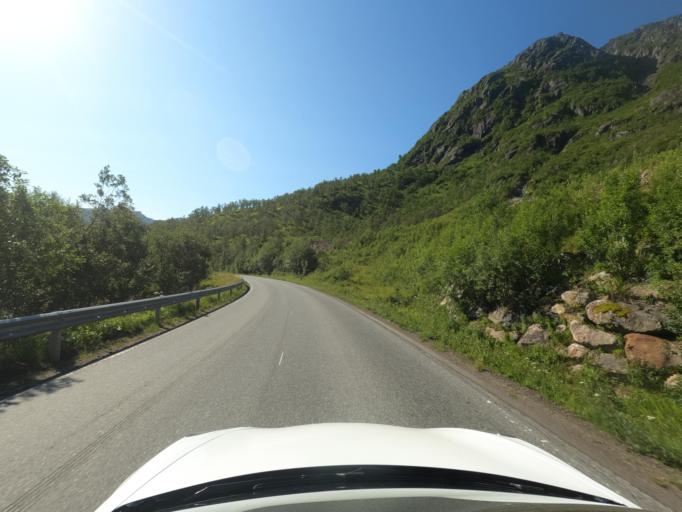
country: NO
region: Nordland
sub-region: Lodingen
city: Lodingen
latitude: 68.5567
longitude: 15.7463
